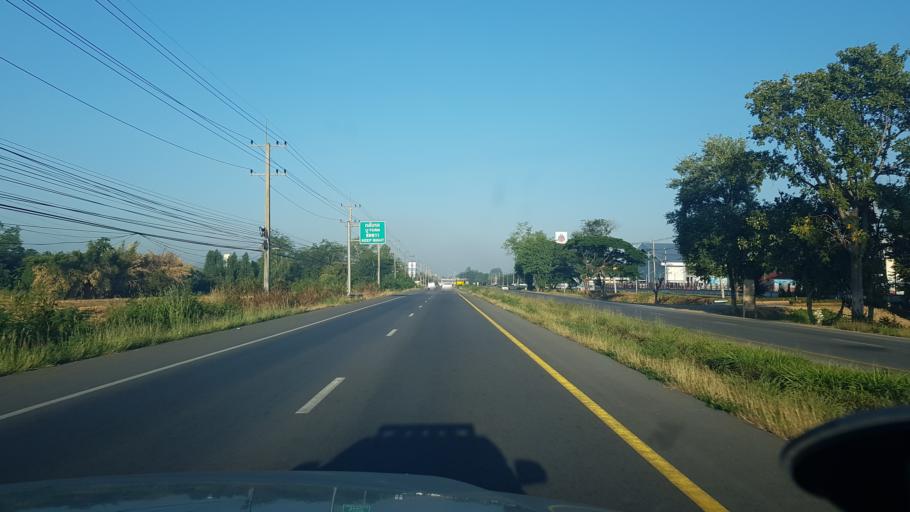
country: TH
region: Khon Kaen
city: Chum Phae
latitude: 16.5820
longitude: 102.0155
